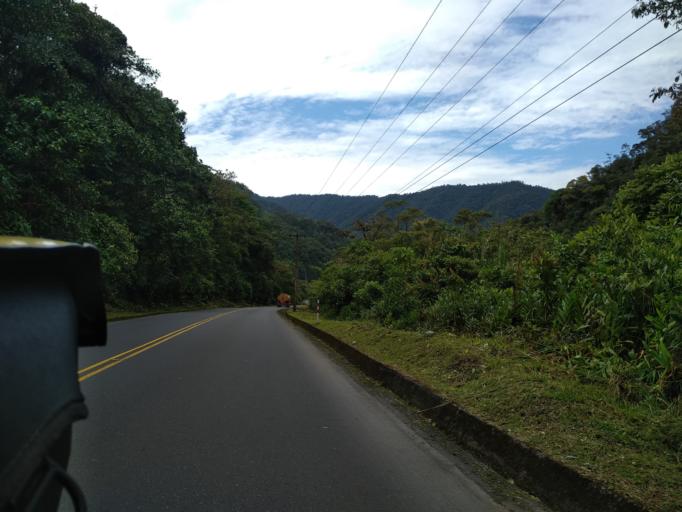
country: EC
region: Pastaza
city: Puyo
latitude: -1.4131
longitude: -78.1841
